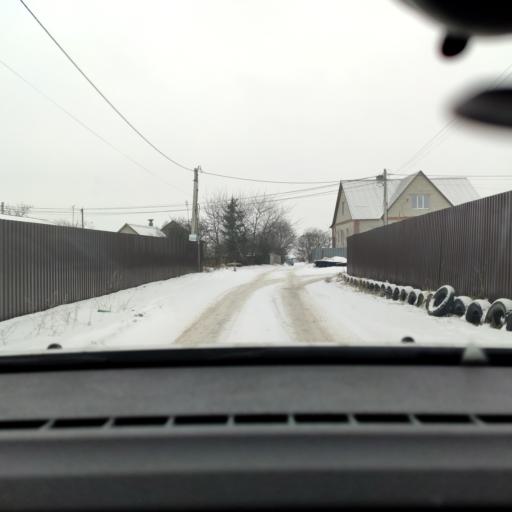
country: RU
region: Voronezj
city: Podgornoye
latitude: 51.7948
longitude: 39.1410
